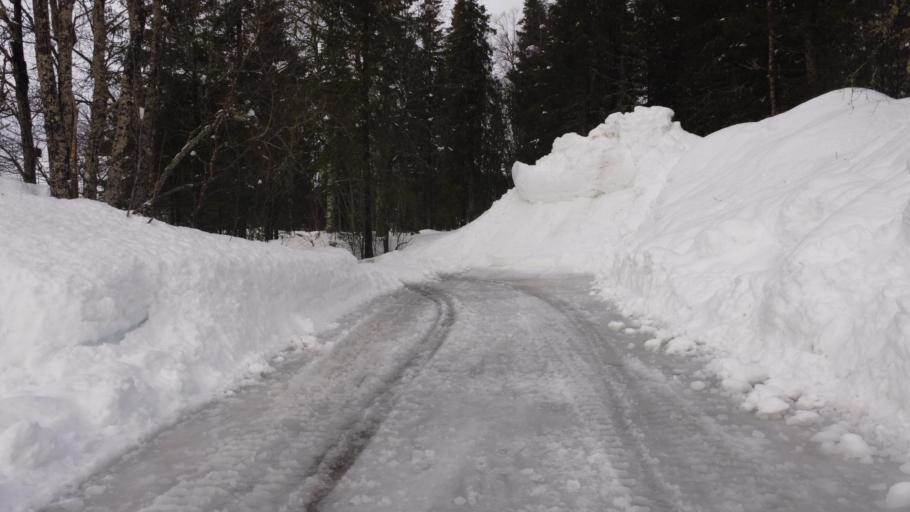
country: NO
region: Nordland
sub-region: Rana
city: Mo i Rana
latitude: 66.3353
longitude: 14.1455
